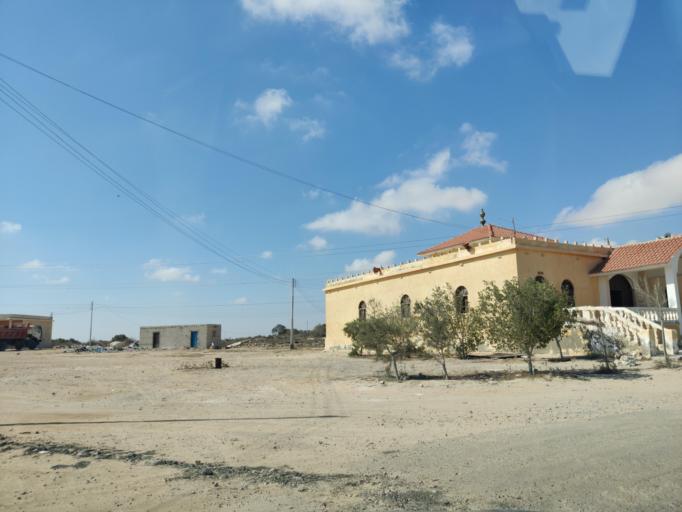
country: EG
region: Muhafazat Matruh
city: Al `Alamayn
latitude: 31.0446
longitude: 28.3462
